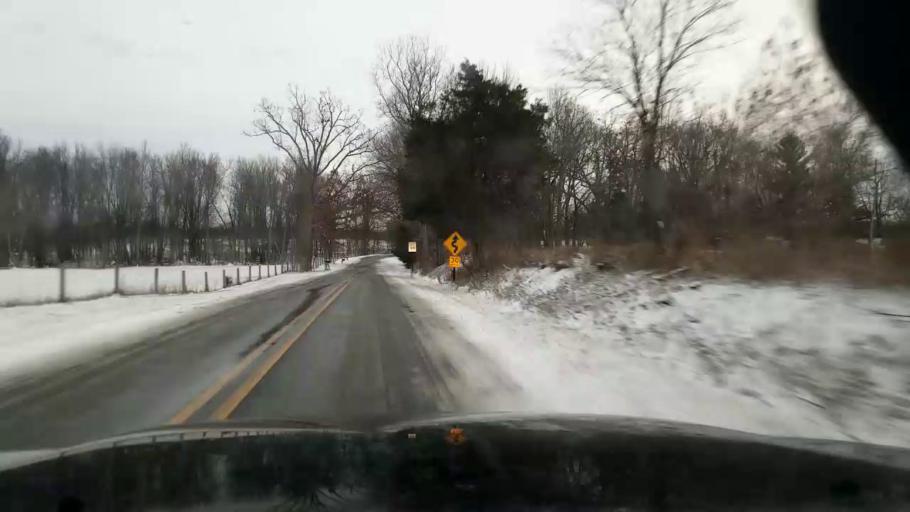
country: US
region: Michigan
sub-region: Jackson County
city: Vandercook Lake
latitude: 42.0894
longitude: -84.4658
